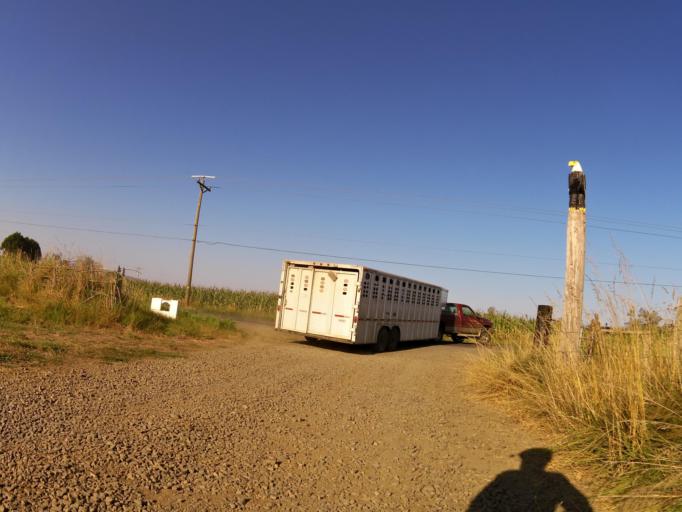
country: US
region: Oregon
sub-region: Tillamook County
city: Tillamook
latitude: 45.4380
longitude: -123.7758
